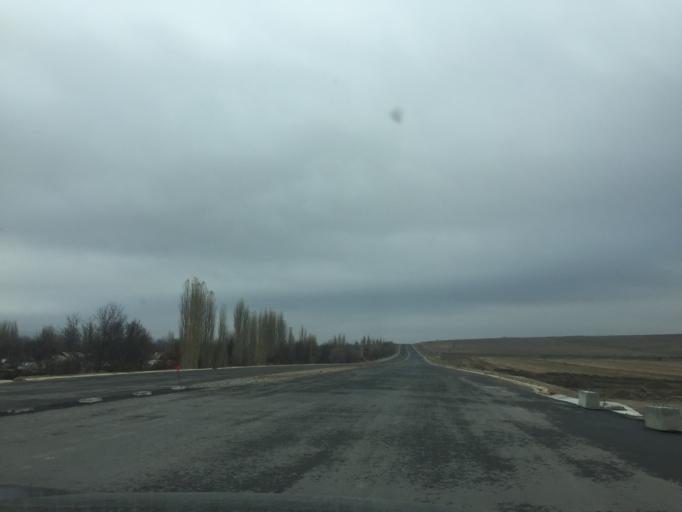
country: KZ
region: Ongtustik Qazaqstan
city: Kokterek
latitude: 42.5496
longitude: 70.1637
